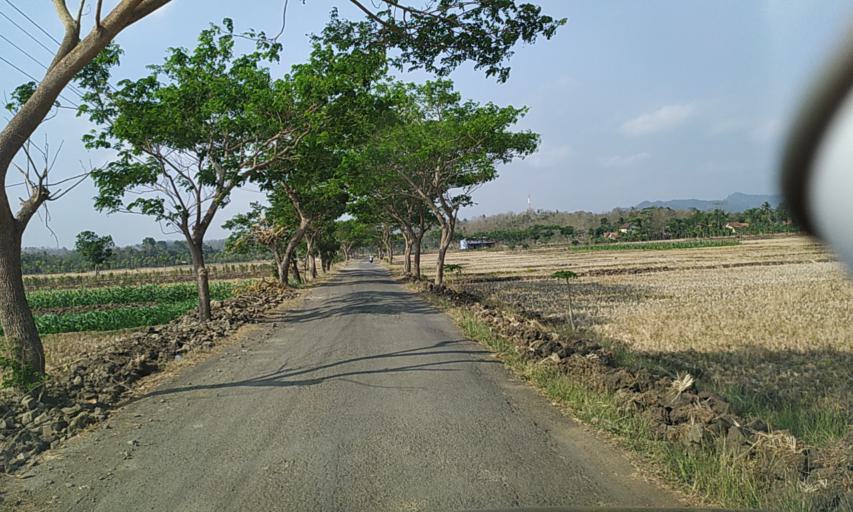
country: ID
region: Central Java
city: Muktisari
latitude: -7.4991
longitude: 108.8875
